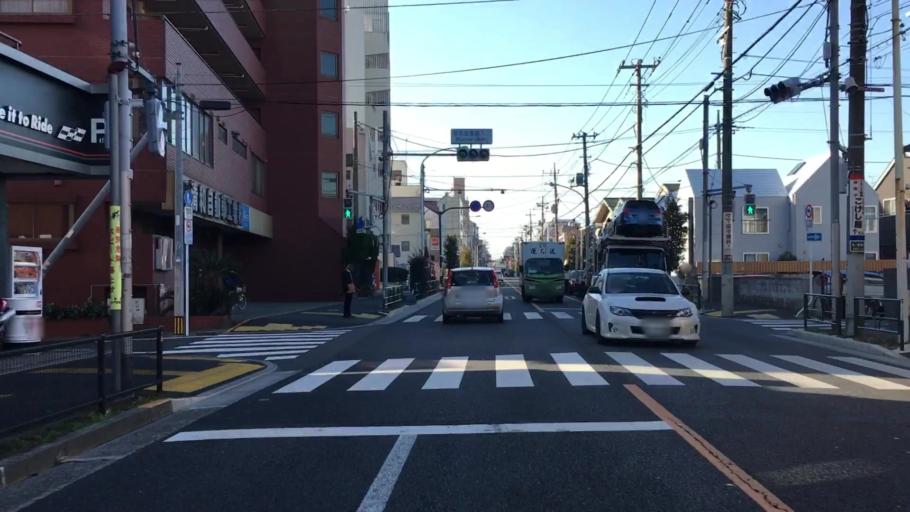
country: JP
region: Tokyo
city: Mitaka-shi
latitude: 35.6947
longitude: 139.5999
